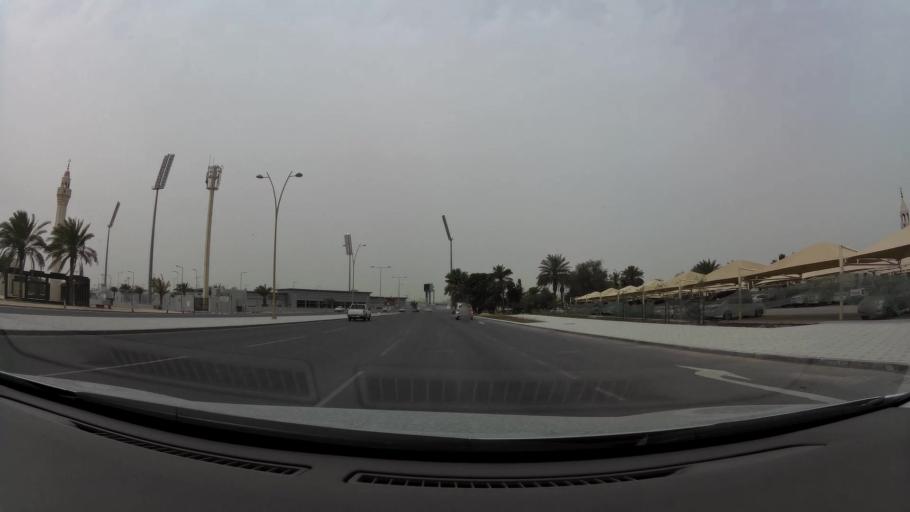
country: QA
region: Baladiyat ad Dawhah
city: Doha
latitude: 25.2510
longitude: 51.5378
